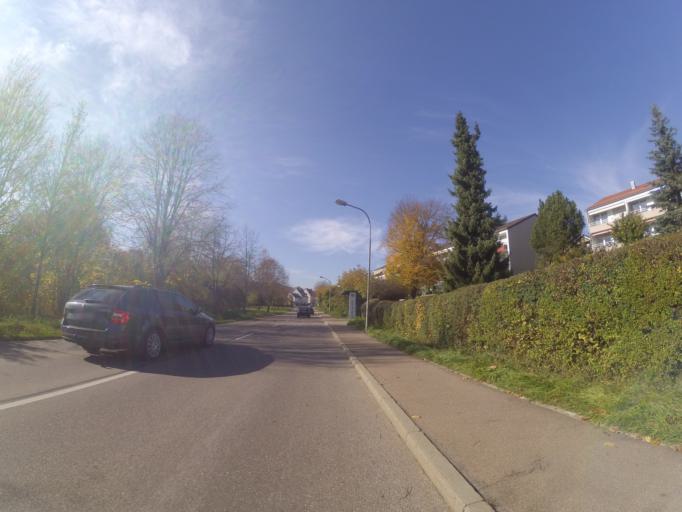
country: DE
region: Baden-Wuerttemberg
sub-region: Tuebingen Region
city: Ulm
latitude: 48.4085
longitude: 9.9351
